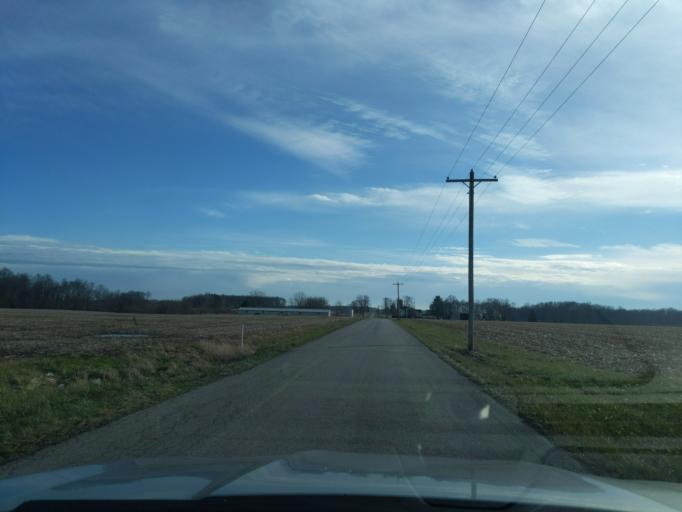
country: US
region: Indiana
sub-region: Decatur County
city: Westport
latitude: 39.2154
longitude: -85.4649
